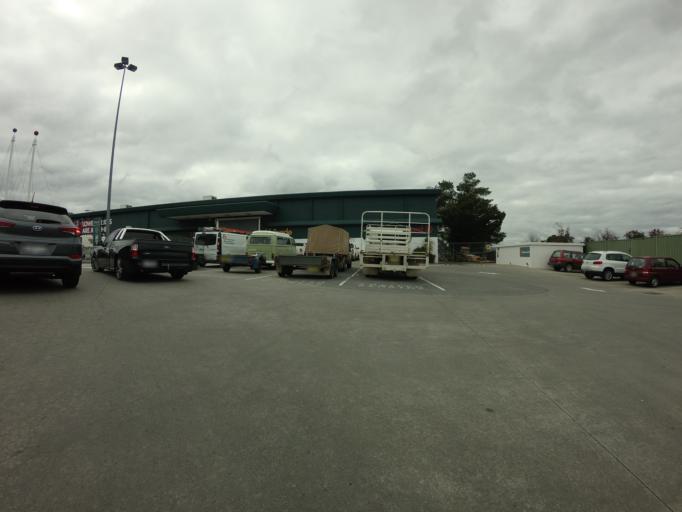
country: AU
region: Australian Capital Territory
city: Forrest
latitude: -35.3317
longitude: 149.1781
